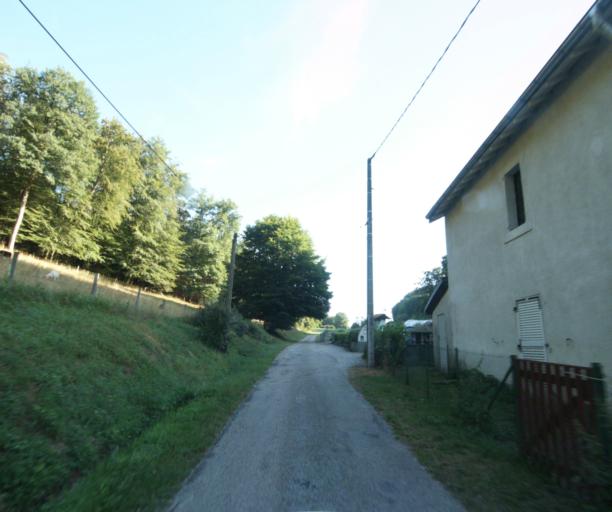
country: FR
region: Lorraine
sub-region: Departement des Vosges
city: Urimenil
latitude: 48.1349
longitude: 6.4196
